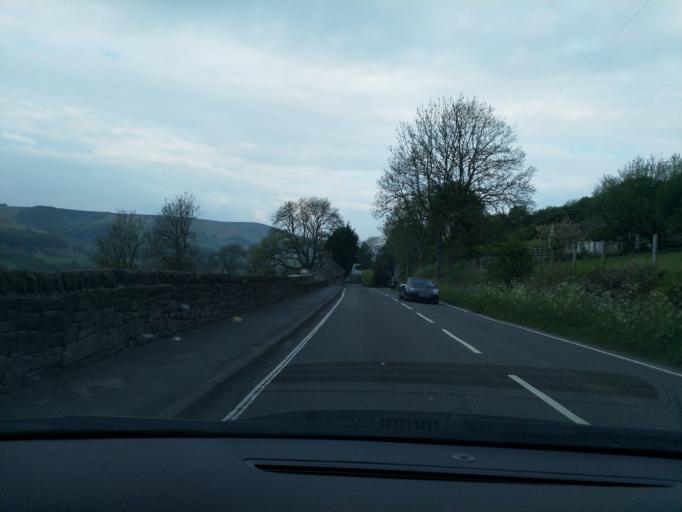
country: GB
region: England
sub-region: Derbyshire
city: Hathersage
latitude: 53.3252
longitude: -1.6427
